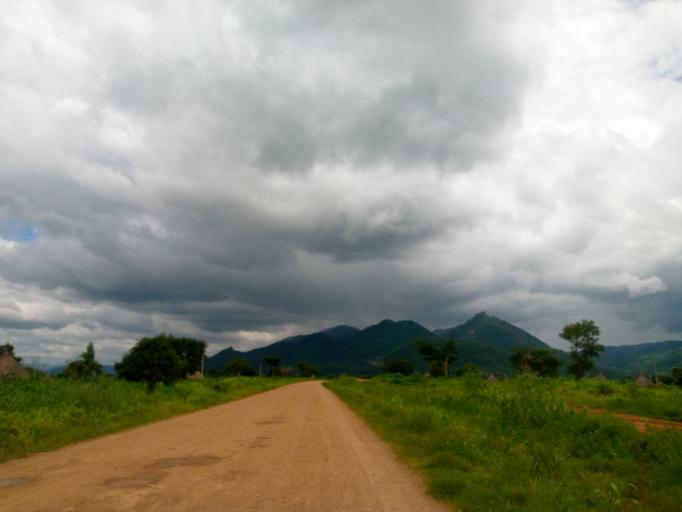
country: ET
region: Oromiya
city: Mendi
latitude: 10.1861
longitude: 35.0931
